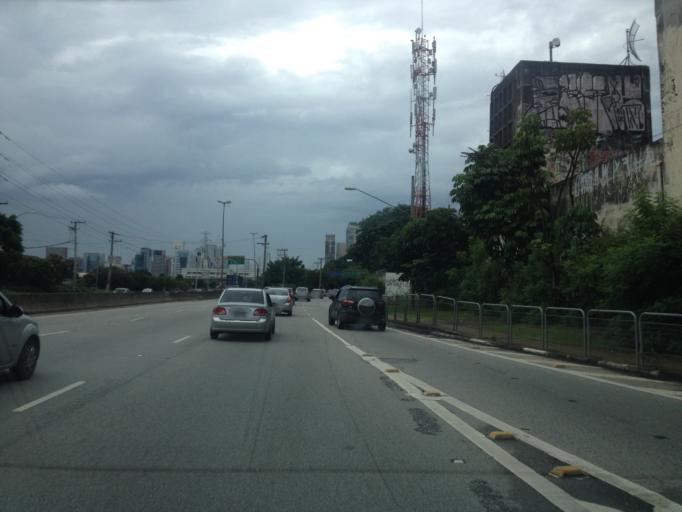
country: BR
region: Sao Paulo
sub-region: Sao Paulo
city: Sao Paulo
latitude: -23.5882
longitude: -46.6927
